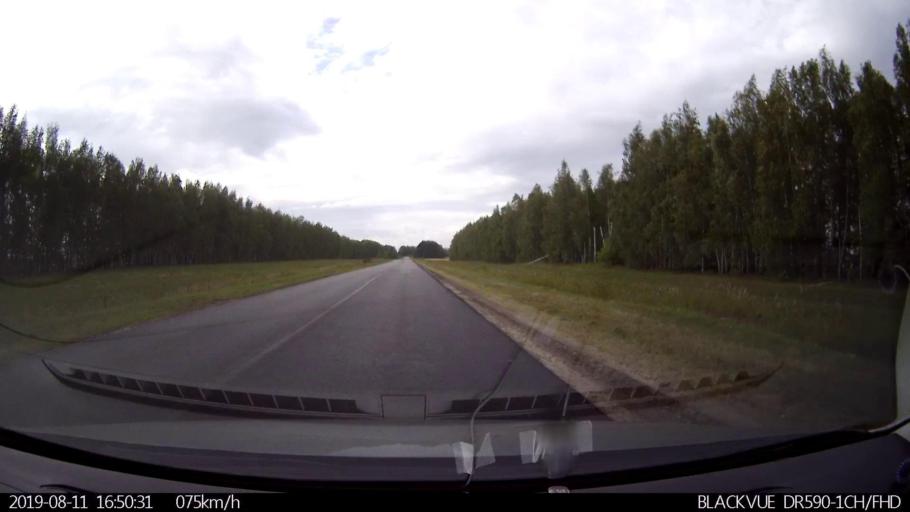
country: RU
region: Ulyanovsk
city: Mayna
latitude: 54.2295
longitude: 47.6865
